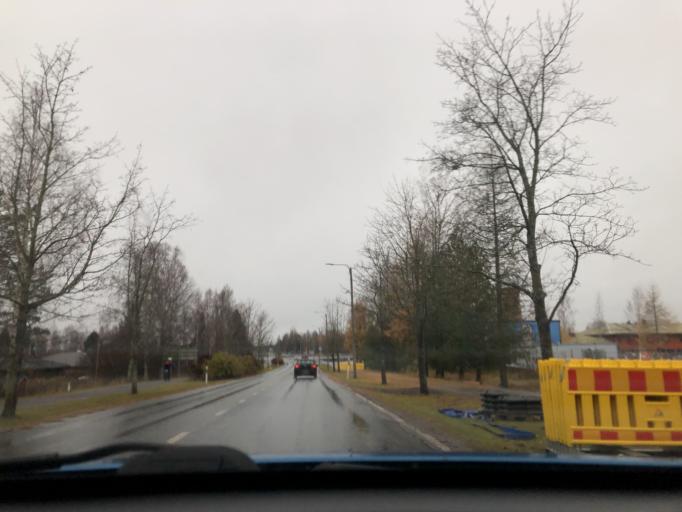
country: FI
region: Pirkanmaa
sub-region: Tampere
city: Kangasala
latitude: 61.4678
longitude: 24.0390
